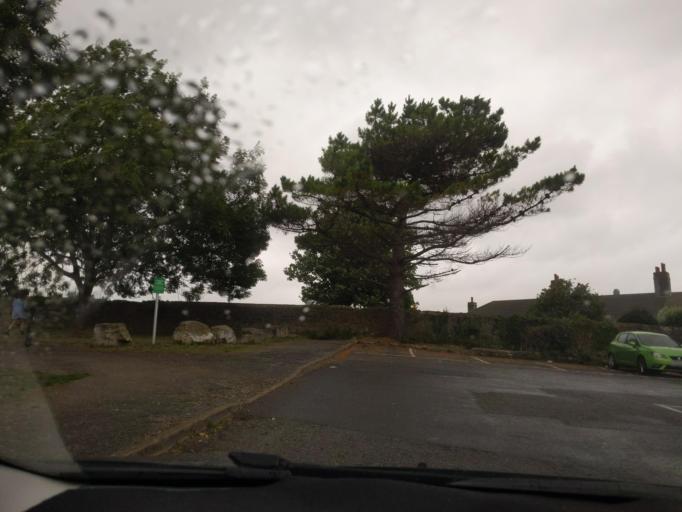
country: GB
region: England
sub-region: Cornwall
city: Millbrook
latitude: 50.3603
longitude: -4.1640
